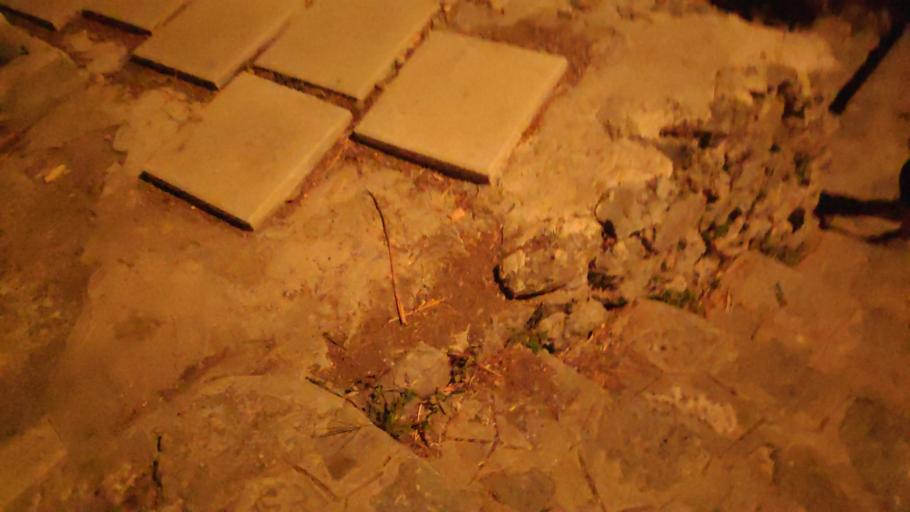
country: IT
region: Campania
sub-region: Provincia di Salerno
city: Ravello
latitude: 40.6484
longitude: 14.6138
